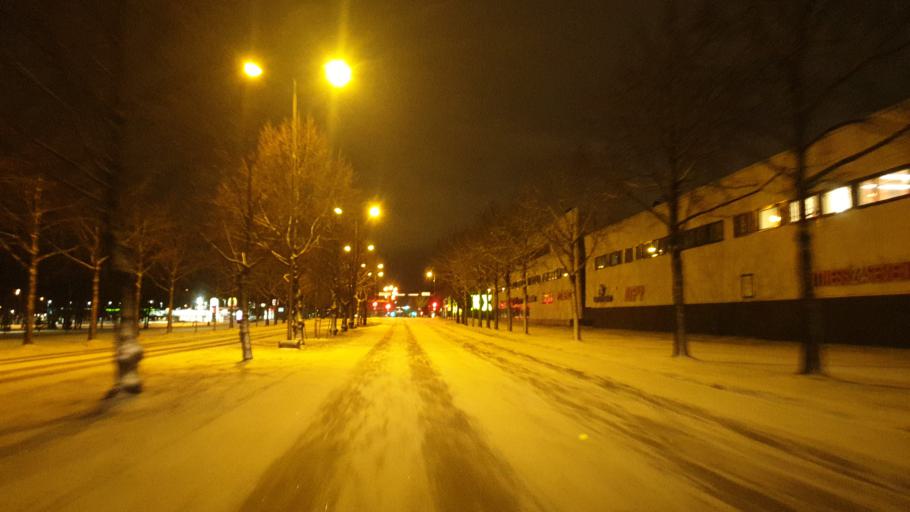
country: FI
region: Northern Ostrobothnia
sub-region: Oulu
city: Oulu
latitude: 64.9945
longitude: 25.4649
